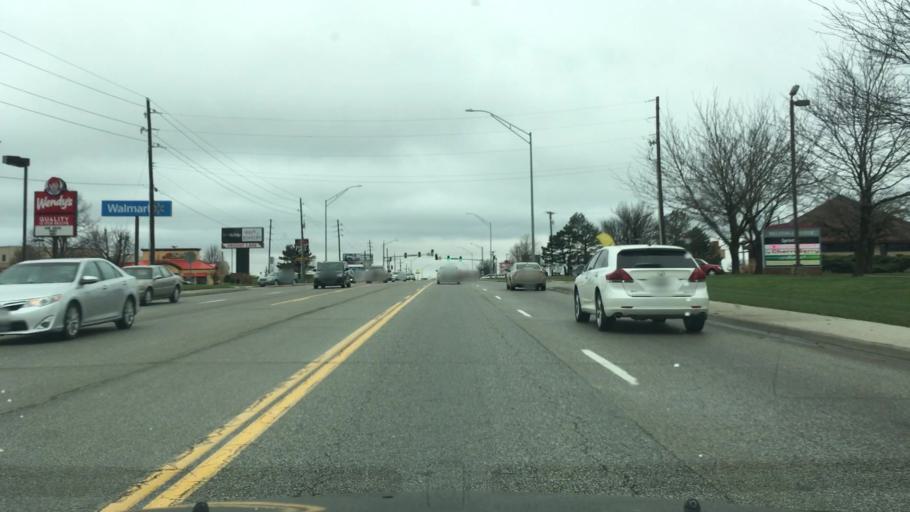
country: US
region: Missouri
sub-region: Cass County
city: Belton
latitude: 38.8129
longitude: -94.4949
